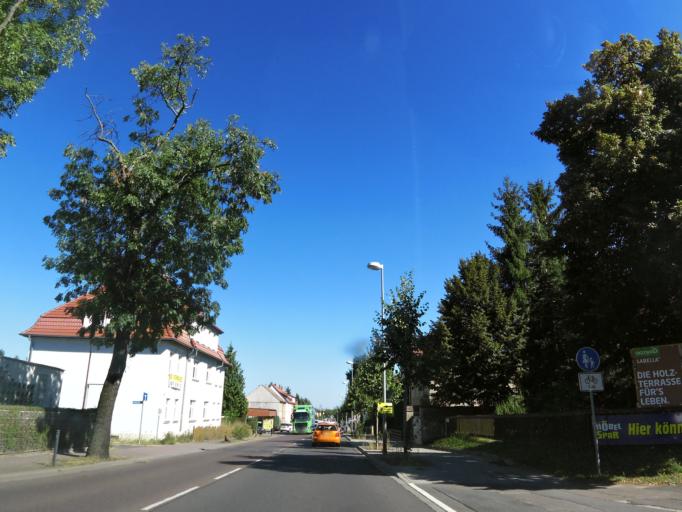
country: DE
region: Saxony
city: Markranstadt
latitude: 51.3468
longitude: 12.2556
